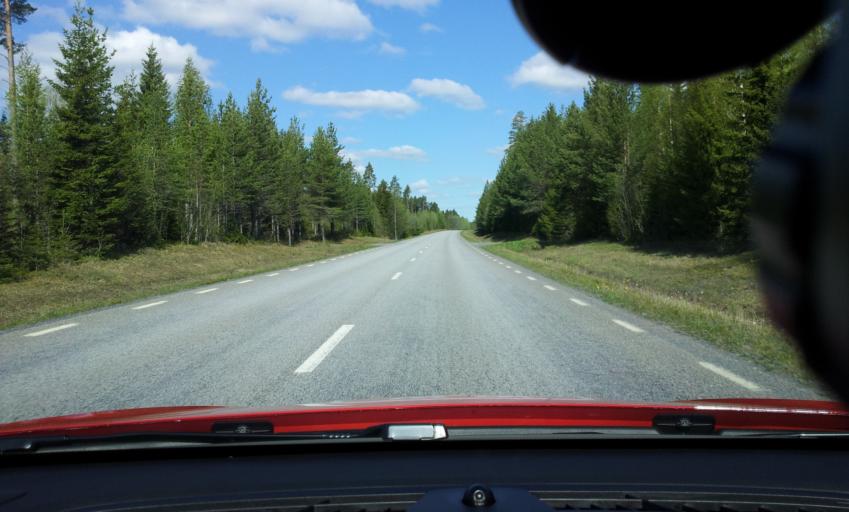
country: SE
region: Jaemtland
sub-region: Krokoms Kommun
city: Valla
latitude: 63.2618
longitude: 13.9748
